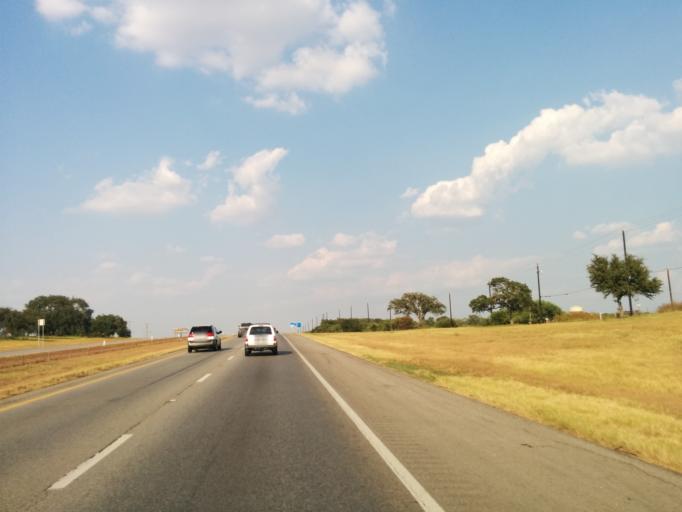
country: US
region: Texas
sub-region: Guadalupe County
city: Schertz
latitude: 29.4839
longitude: -98.2352
